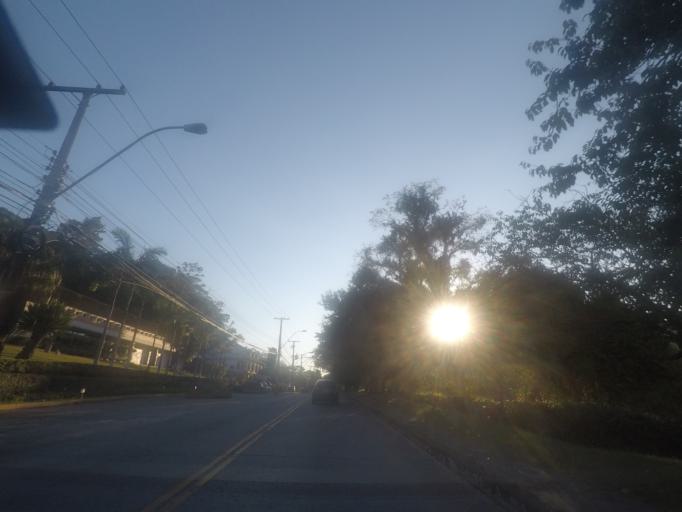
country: BR
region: Rio de Janeiro
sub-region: Petropolis
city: Petropolis
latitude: -22.5303
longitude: -43.2143
